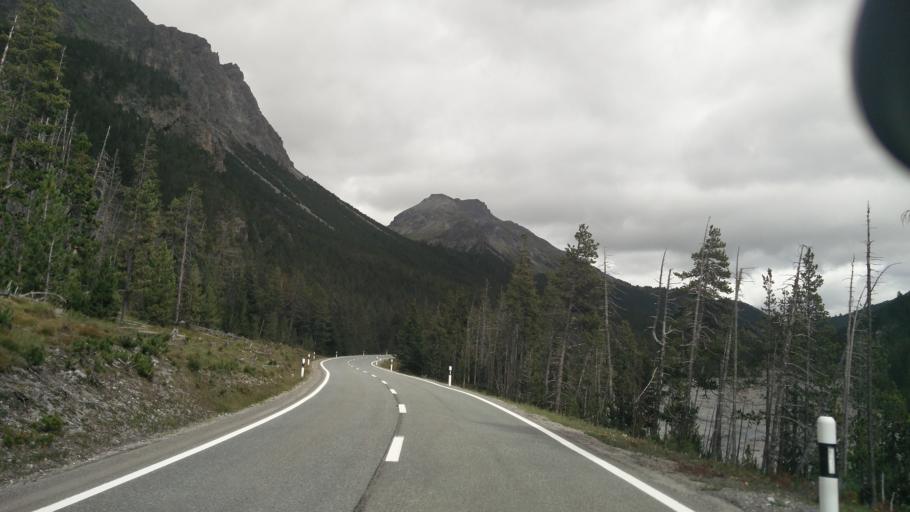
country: CH
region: Grisons
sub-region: Inn District
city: Scuol
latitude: 46.6538
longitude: 10.2511
